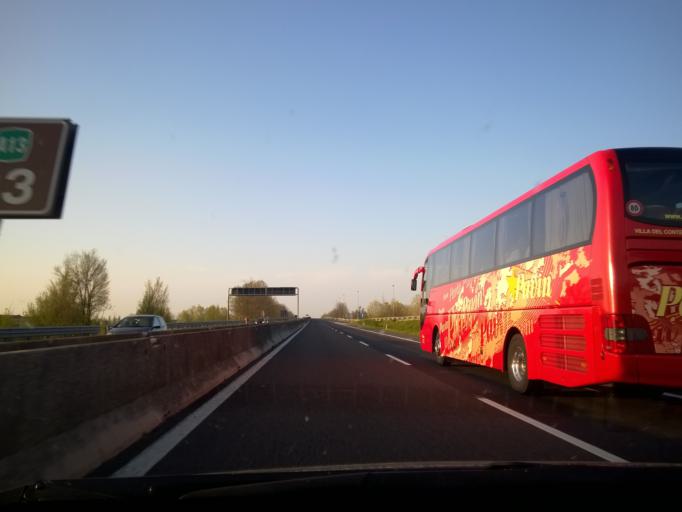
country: IT
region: Emilia-Romagna
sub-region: Provincia di Ferrara
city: San Martino
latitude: 44.7957
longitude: 11.5529
